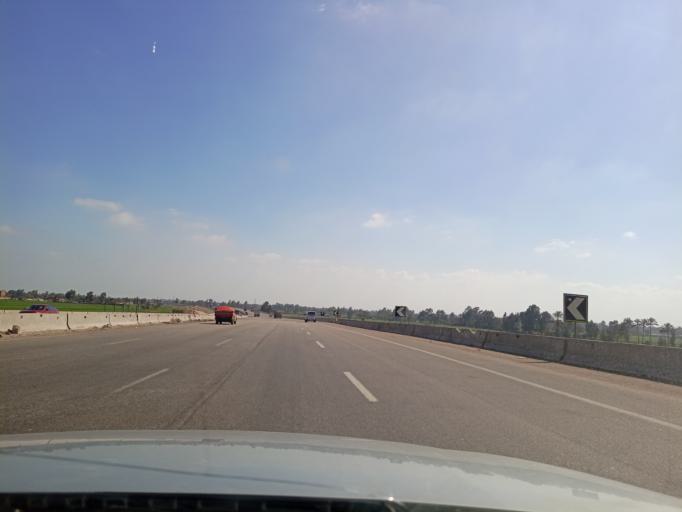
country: EG
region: Eastern Province
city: Mashtul as Suq
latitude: 30.4600
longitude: 31.3335
